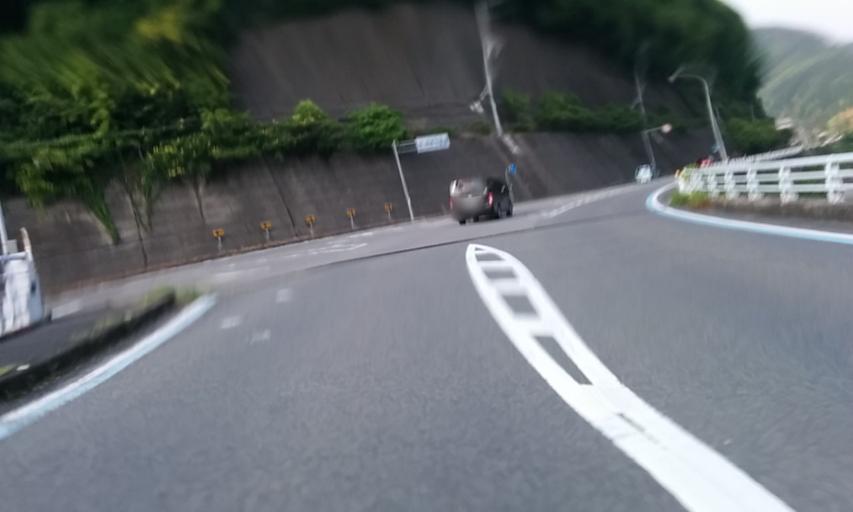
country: JP
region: Ehime
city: Saijo
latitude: 33.8877
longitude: 133.1833
